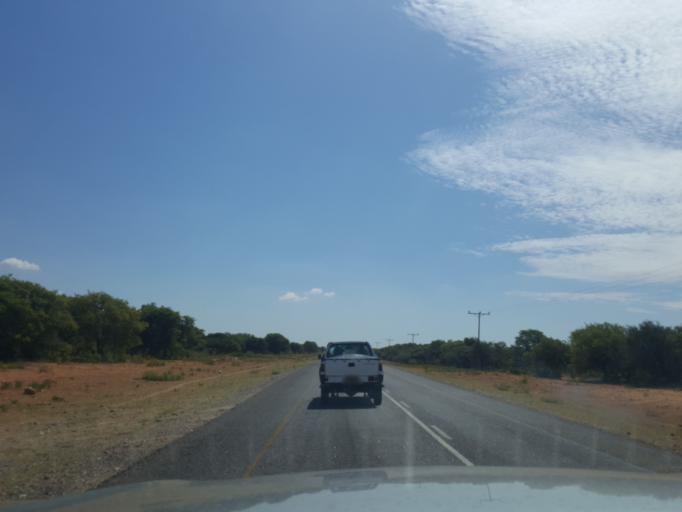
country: BW
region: Kweneng
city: Letlhakeng
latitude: -24.1238
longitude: 25.0964
